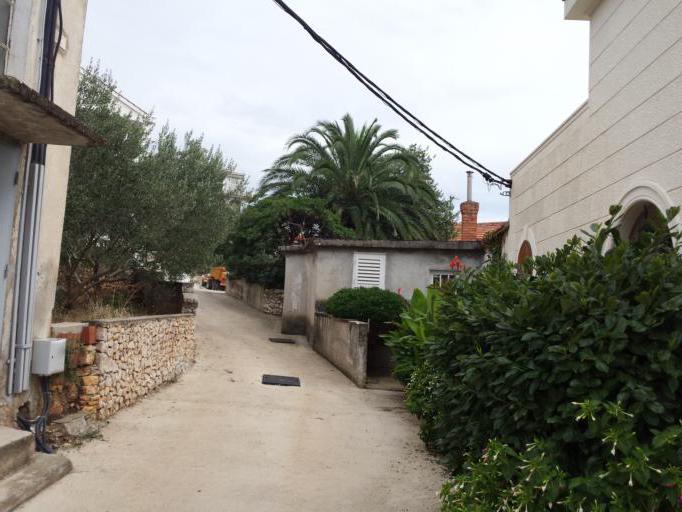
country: HR
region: Sibensko-Kniniska
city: Rogoznica
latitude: 43.5273
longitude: 15.9693
